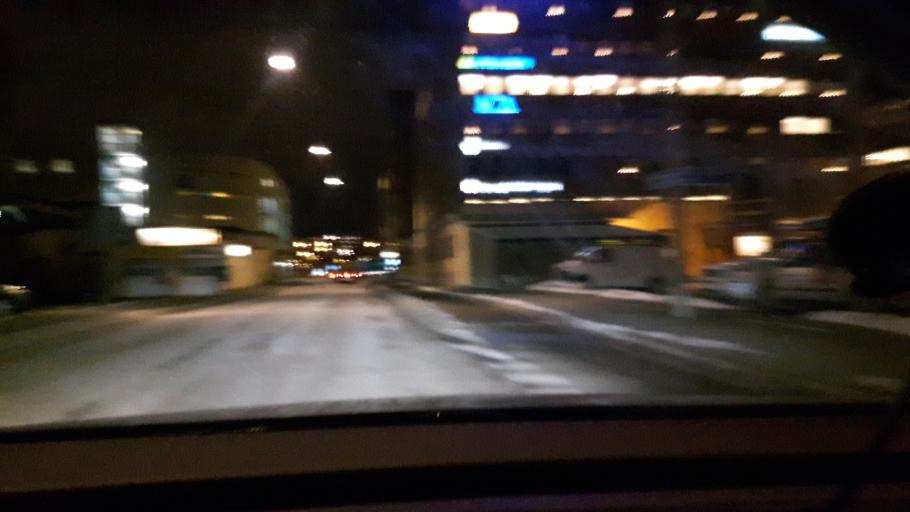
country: SE
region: Vaestra Goetaland
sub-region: Goteborg
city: Goeteborg
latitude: 57.7000
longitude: 11.9432
